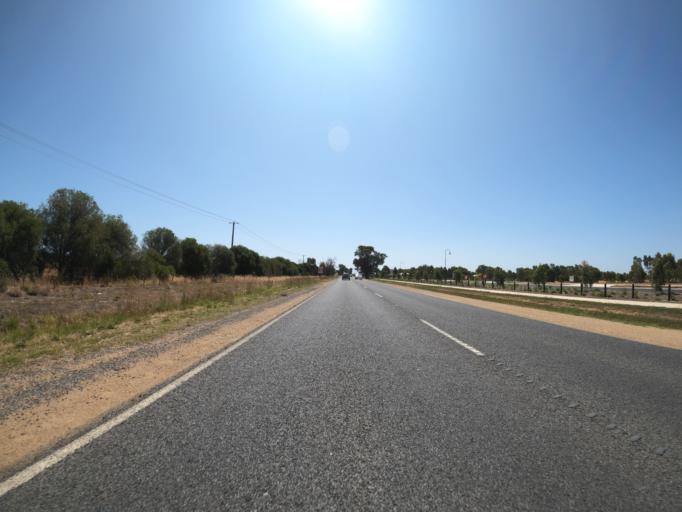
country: AU
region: Victoria
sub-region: Moira
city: Yarrawonga
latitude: -36.0137
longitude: 146.0402
